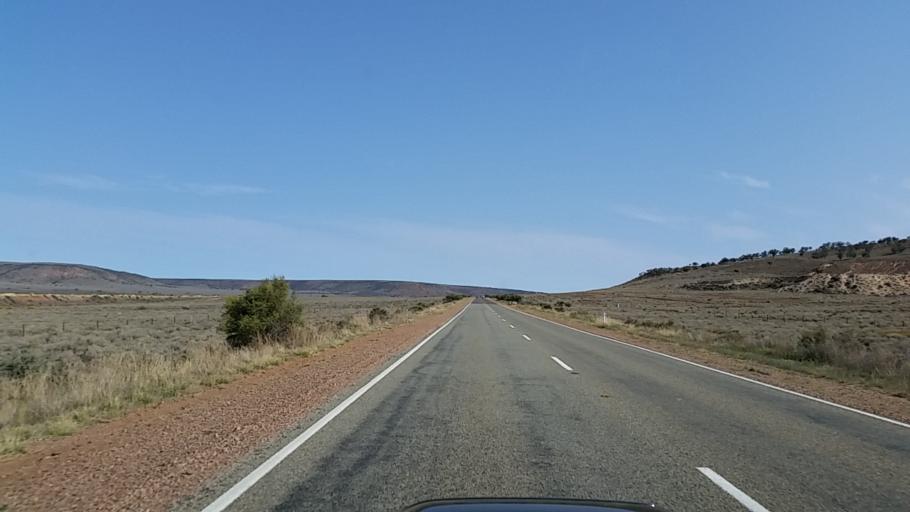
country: AU
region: South Australia
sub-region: Port Augusta
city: Port Augusta West
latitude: -32.5685
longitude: 137.6263
